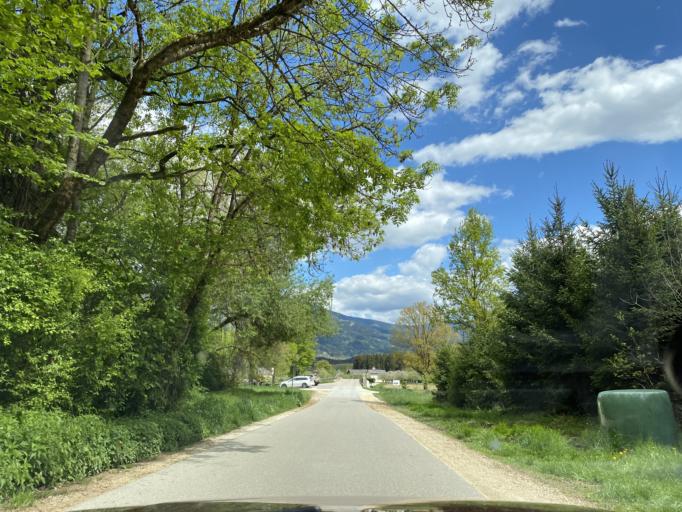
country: AT
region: Carinthia
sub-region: Politischer Bezirk Wolfsberg
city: Sankt Andrae
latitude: 46.7839
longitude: 14.8344
